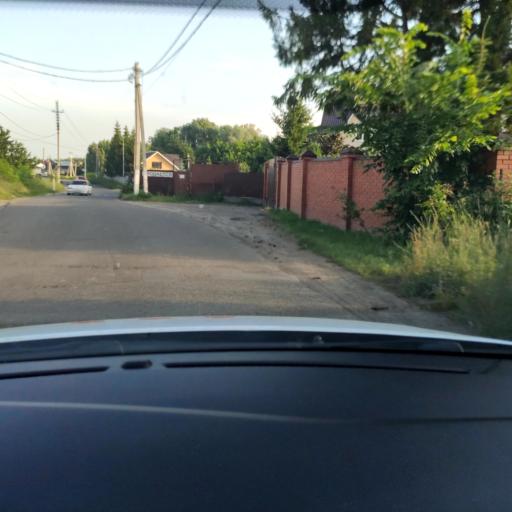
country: RU
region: Tatarstan
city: Vysokaya Gora
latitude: 55.9754
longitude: 49.3061
